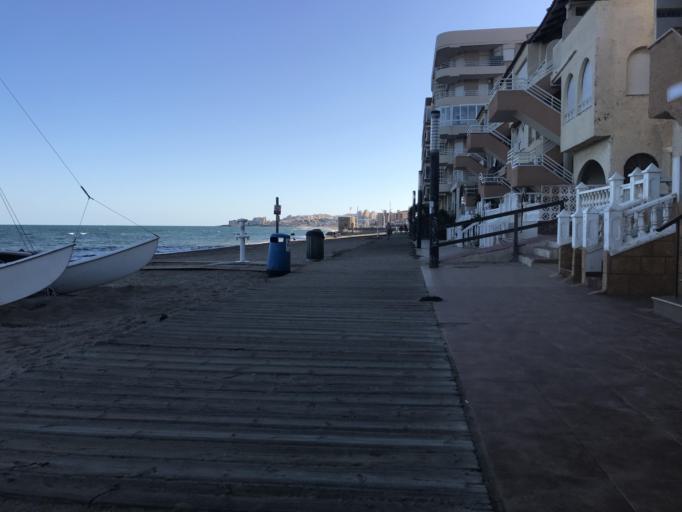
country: ES
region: Valencia
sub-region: Provincia de Alicante
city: Torrevieja
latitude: 38.0284
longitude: -0.6524
